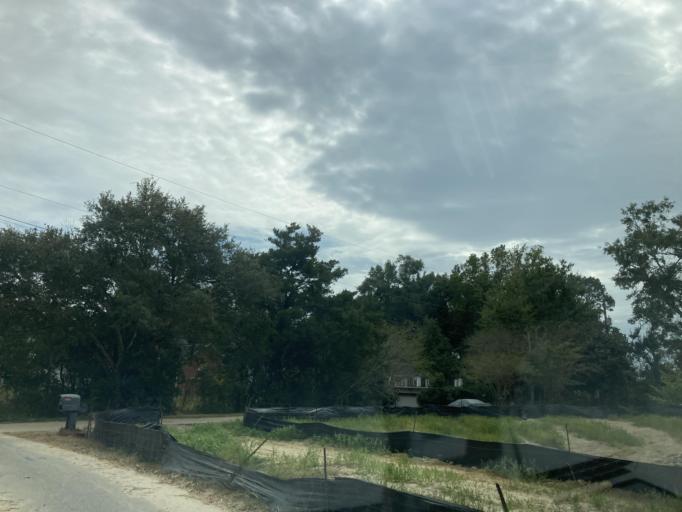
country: US
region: Mississippi
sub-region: Jackson County
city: Gulf Hills
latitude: 30.4327
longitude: -88.8367
